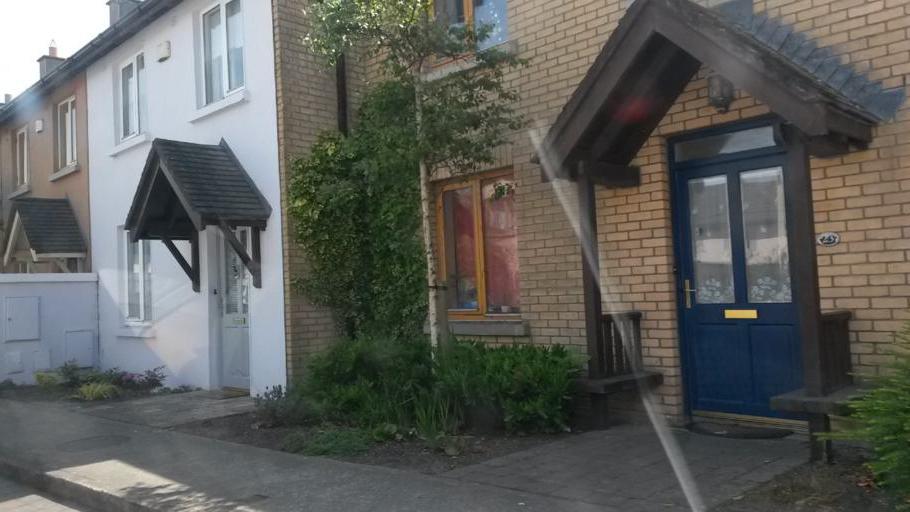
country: IE
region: Leinster
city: Lusk
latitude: 53.5274
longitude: -6.1601
